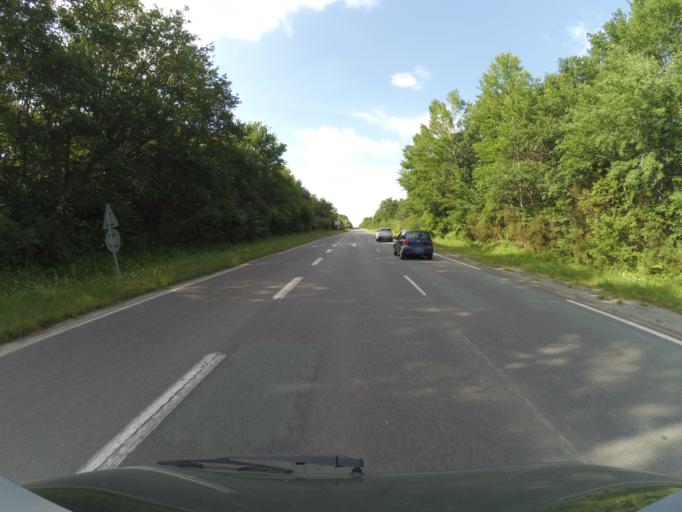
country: FR
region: Poitou-Charentes
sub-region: Departement de la Charente-Maritime
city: Le Gua
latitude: 45.7855
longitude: -0.9362
